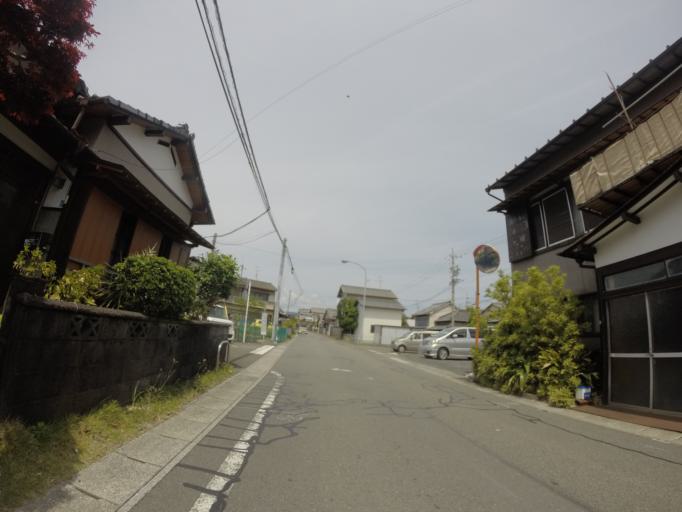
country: JP
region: Shizuoka
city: Yaizu
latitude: 34.8434
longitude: 138.3294
